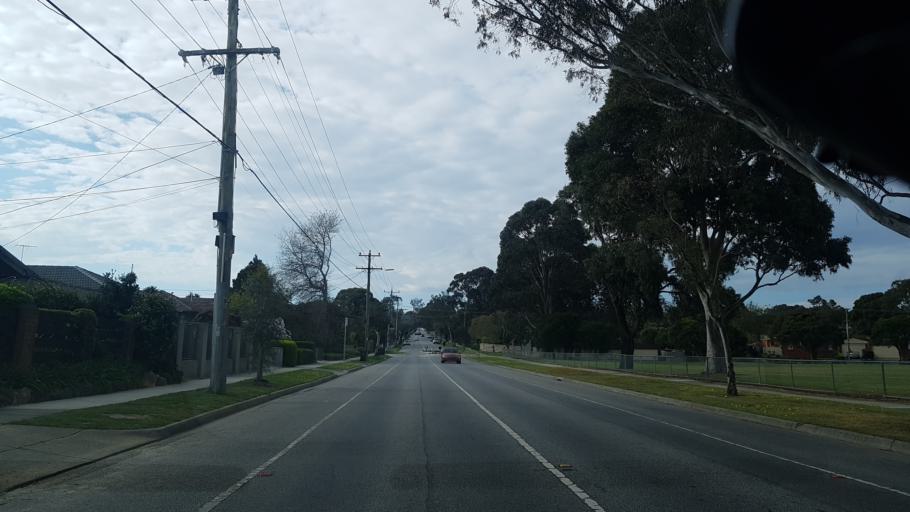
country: AU
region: Victoria
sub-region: Monash
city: Mulgrave
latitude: -37.9097
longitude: 145.1790
